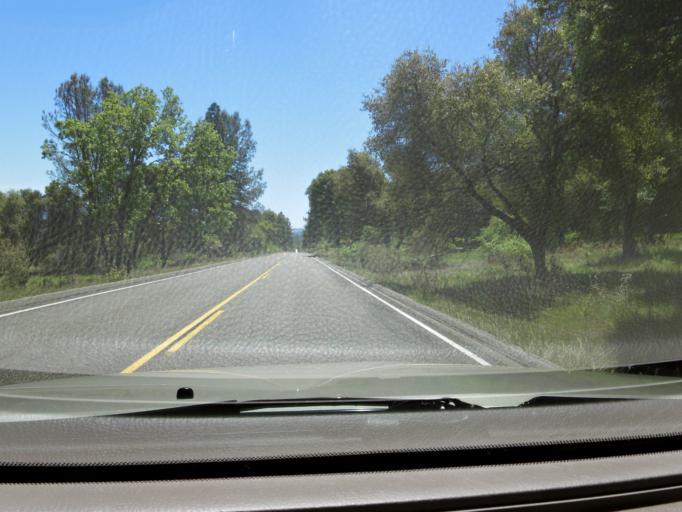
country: US
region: California
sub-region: Fresno County
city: Auberry
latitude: 37.2437
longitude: -119.5051
